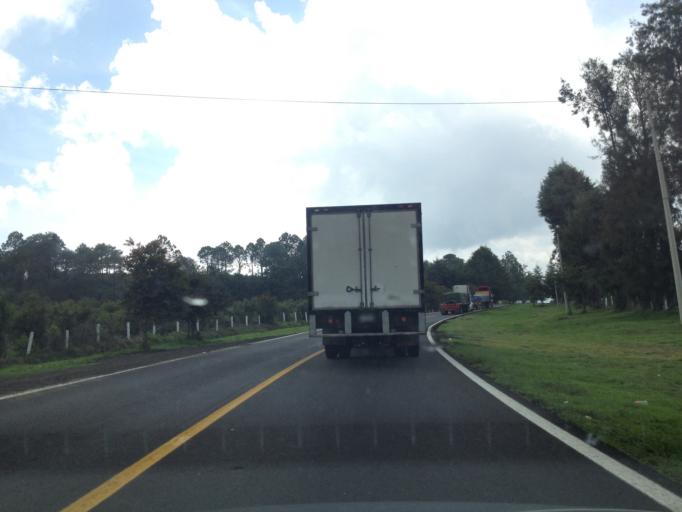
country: MX
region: Michoacan
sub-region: Patzcuaro
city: Santa Maria Huiramangaro (San Juan Tumbio)
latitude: 19.4931
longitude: -101.7483
